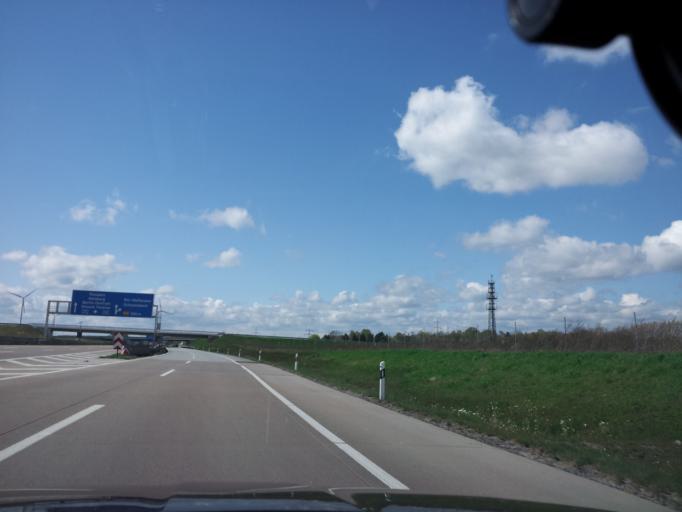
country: DE
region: Brandenburg
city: Ahrensfelde
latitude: 52.6122
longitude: 13.5739
